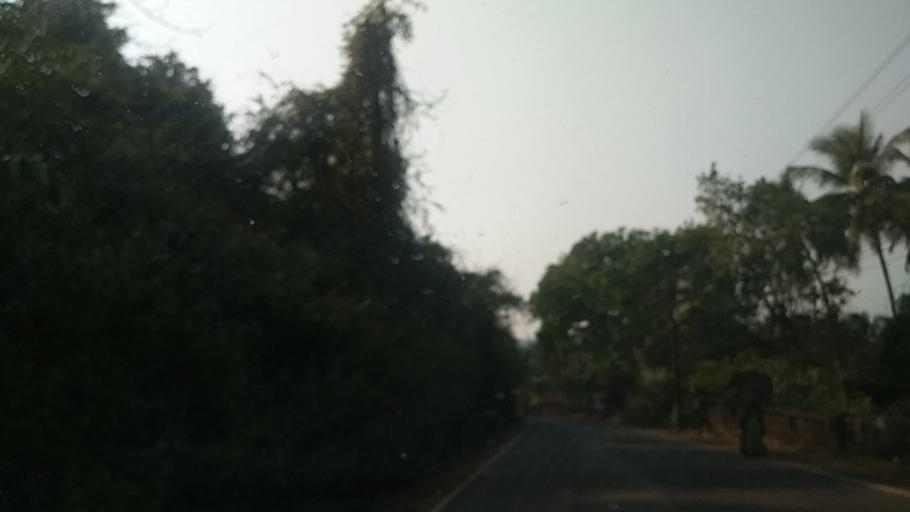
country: IN
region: Goa
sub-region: North Goa
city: Pernem
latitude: 15.7164
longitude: 73.8017
